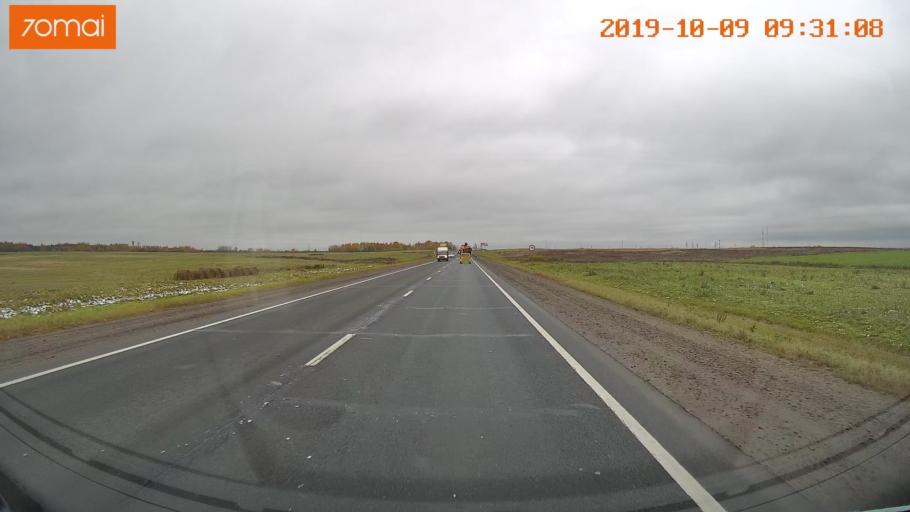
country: RU
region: Vologda
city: Vologda
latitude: 59.1469
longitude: 39.9416
